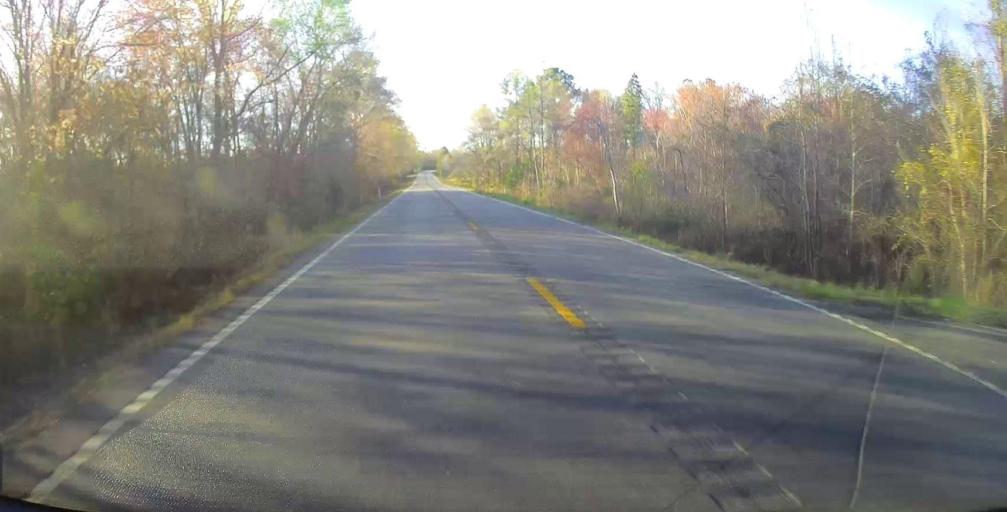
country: US
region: Georgia
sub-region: Wilcox County
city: Abbeville
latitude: 32.1190
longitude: -83.3262
